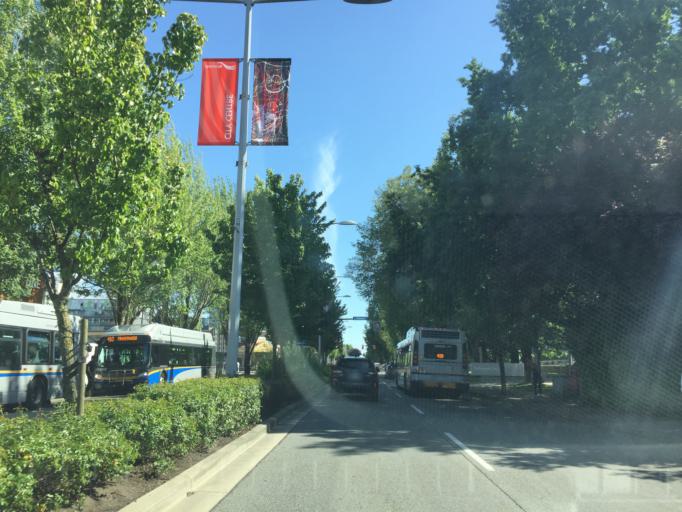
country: CA
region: British Columbia
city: Richmond
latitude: 49.1644
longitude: -123.1367
